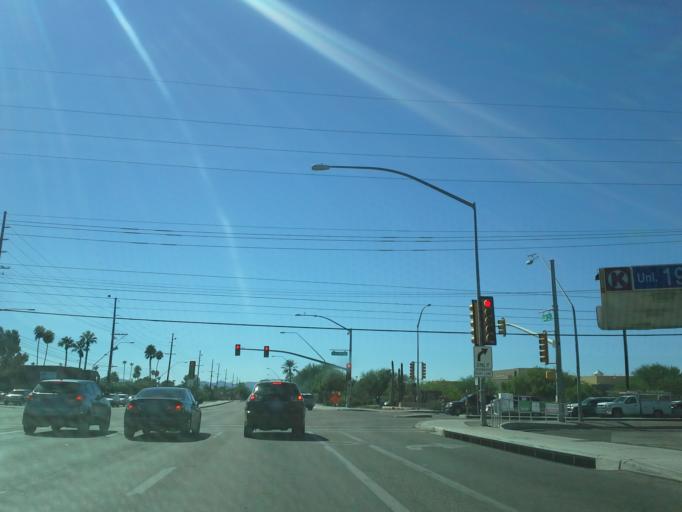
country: US
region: Arizona
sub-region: Pima County
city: Tucson
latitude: 32.2508
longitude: -110.8748
